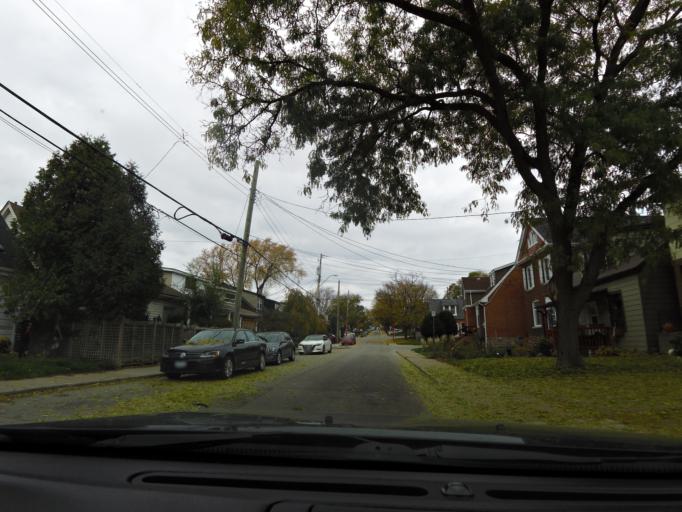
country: CA
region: Ontario
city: Hamilton
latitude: 43.2647
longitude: -79.8886
